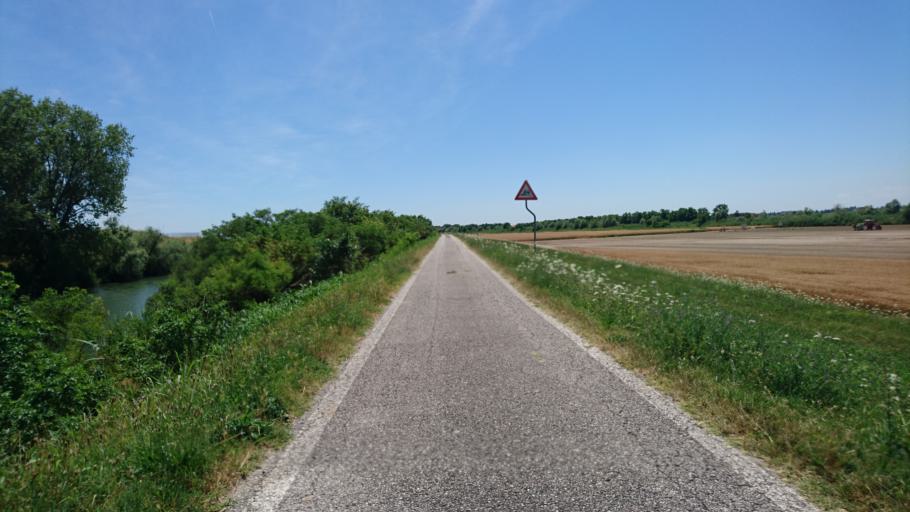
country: IT
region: Veneto
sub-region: Provincia di Venezia
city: Valli
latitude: 45.2180
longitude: 12.1631
